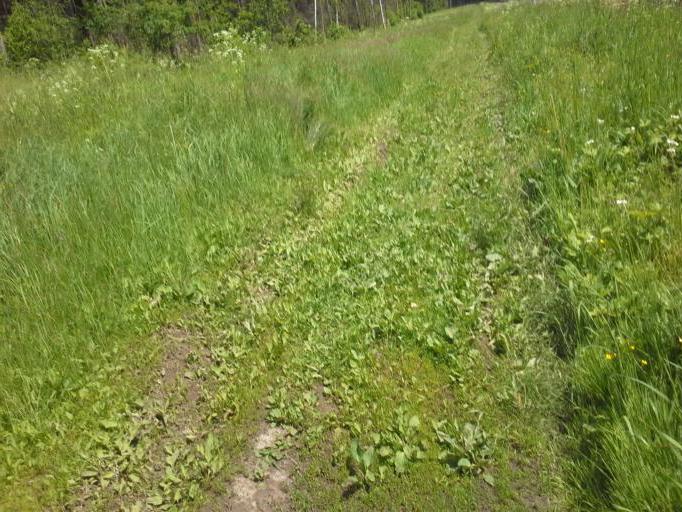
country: RU
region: Moscow
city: Tolstopal'tsevo
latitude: 55.6213
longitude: 37.2311
